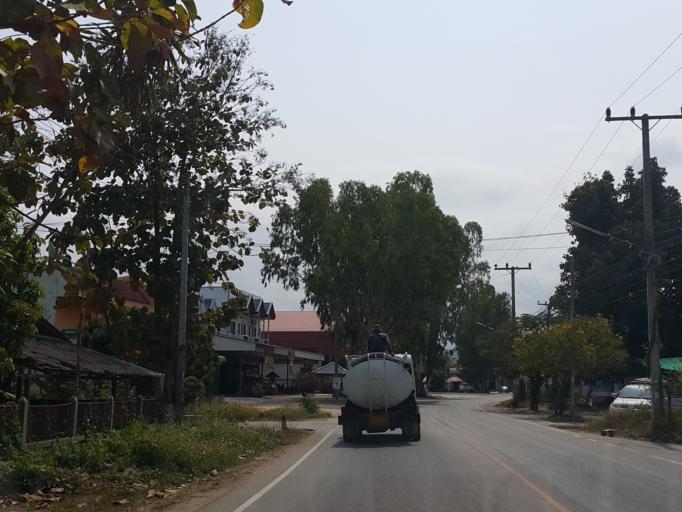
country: TH
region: Lamphun
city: Ban Thi
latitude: 18.6518
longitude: 99.1229
